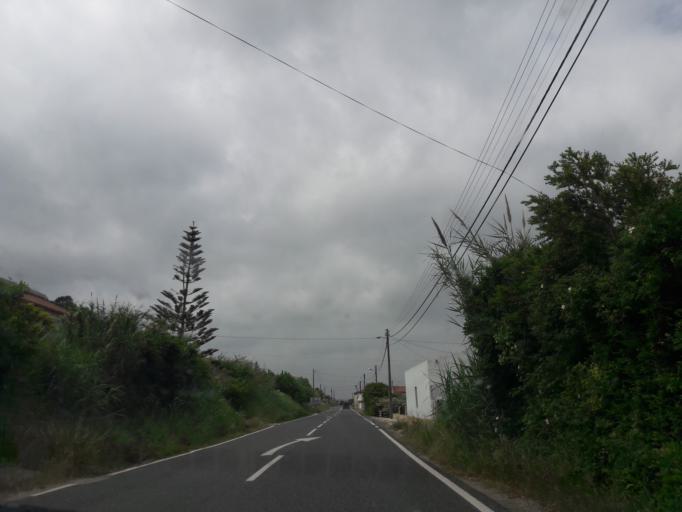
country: PT
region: Leiria
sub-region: Obidos
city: Obidos
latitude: 39.3451
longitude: -9.1653
